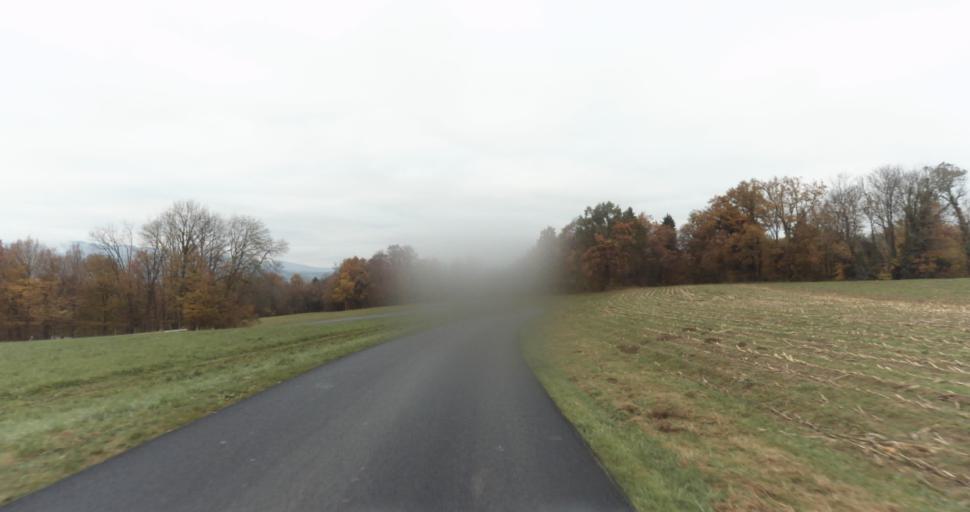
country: FR
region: Rhone-Alpes
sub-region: Departement de la Savoie
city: Albens
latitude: 45.7587
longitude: 5.9701
